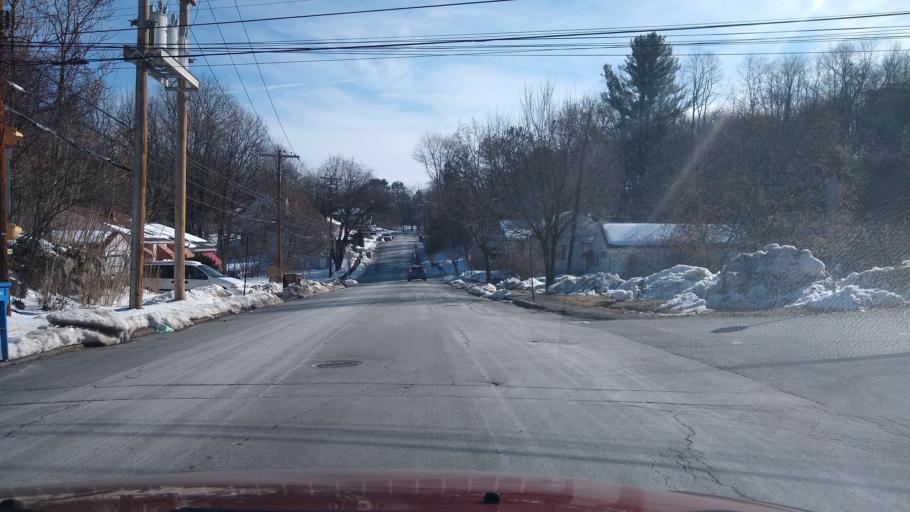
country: US
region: New York
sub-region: Ulster County
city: Kingston
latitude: 41.9216
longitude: -73.9982
